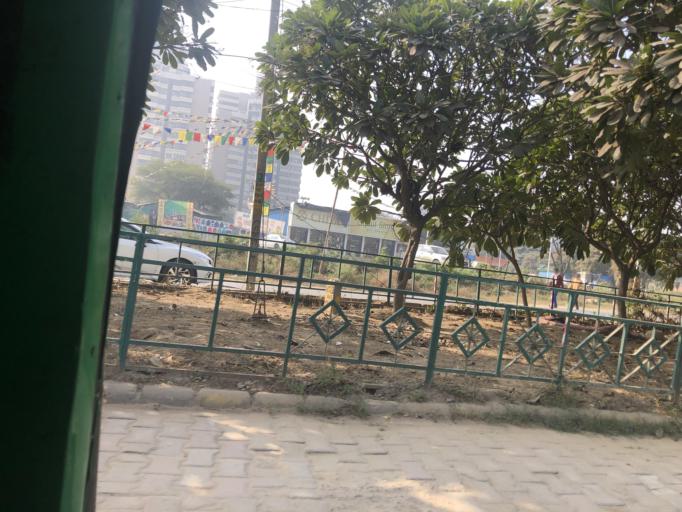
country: IN
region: Haryana
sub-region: Gurgaon
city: Gurgaon
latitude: 28.4469
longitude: 77.0798
